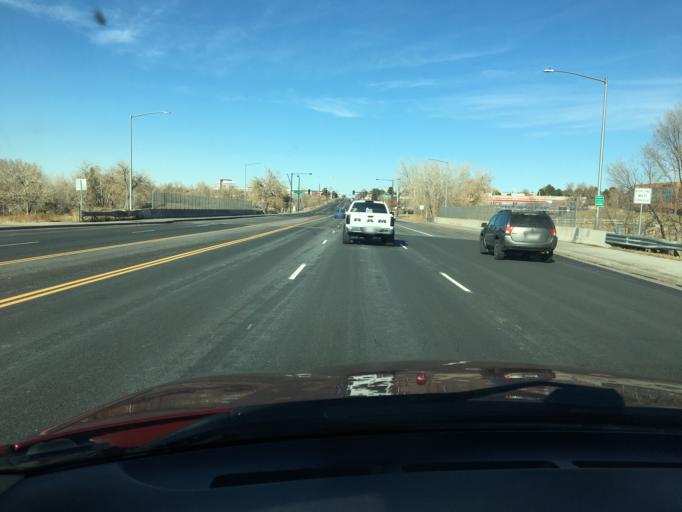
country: US
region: Colorado
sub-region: Adams County
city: Aurora
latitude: 39.6588
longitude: -104.8663
